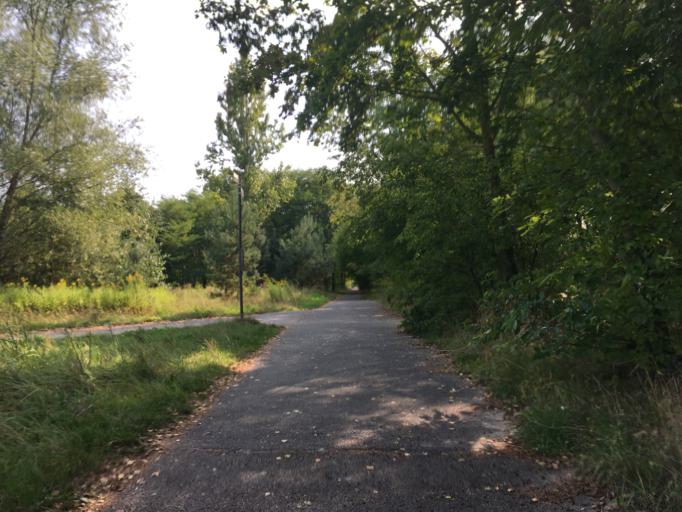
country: DE
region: Berlin
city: Frohnau
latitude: 52.6481
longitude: 13.2836
